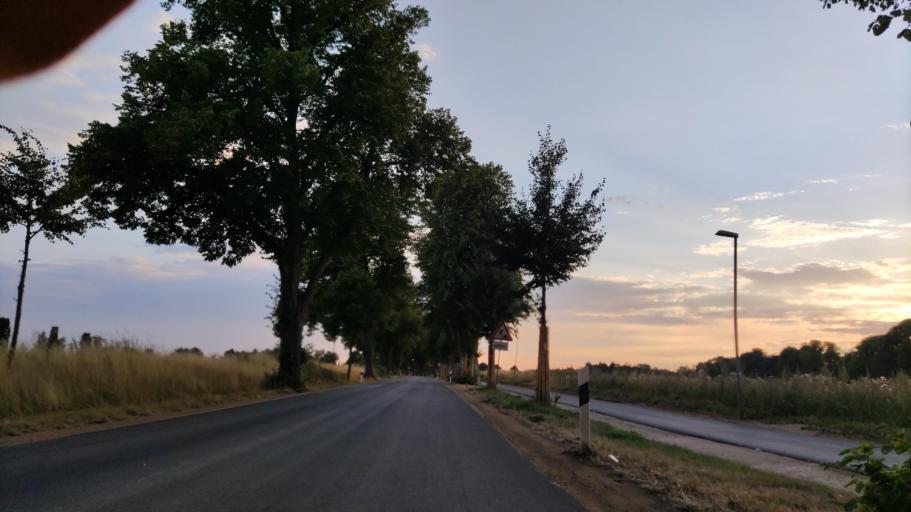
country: DE
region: Lower Saxony
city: Reppenstedt
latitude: 53.2480
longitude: 10.3762
